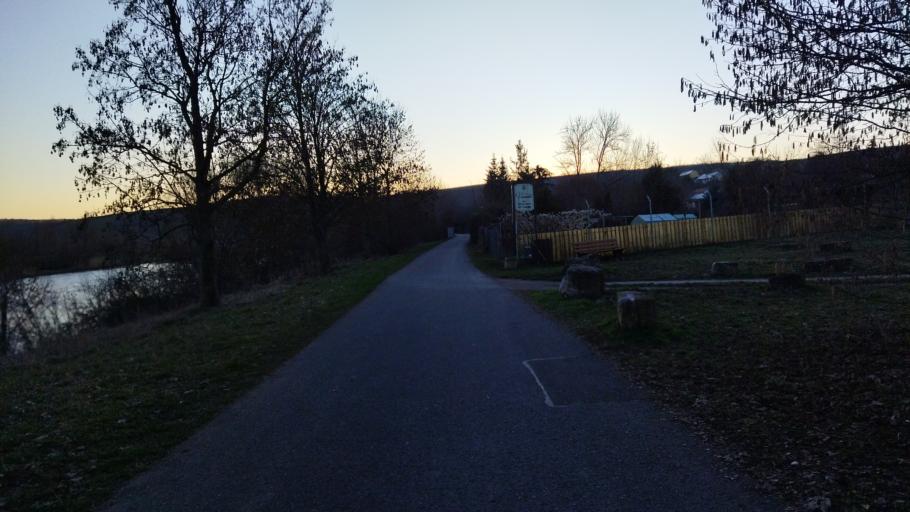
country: DE
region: Bavaria
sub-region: Regierungsbezirk Unterfranken
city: Dettelbach
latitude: 49.8001
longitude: 10.1630
